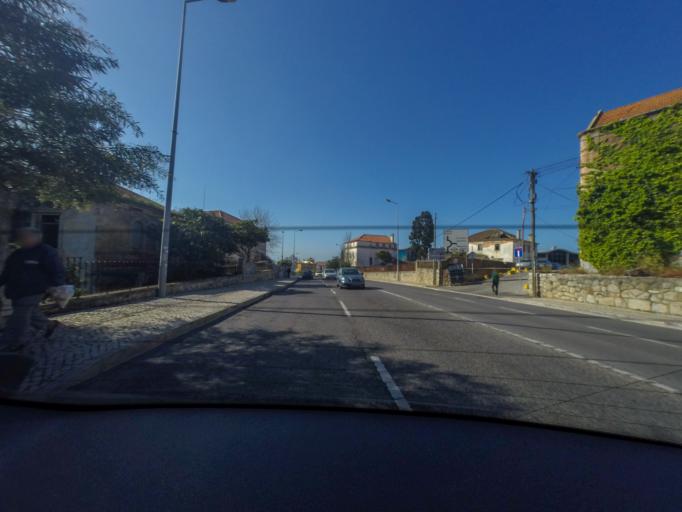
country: PT
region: Lisbon
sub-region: Cascais
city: Monte Estoril
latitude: 38.7027
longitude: -9.4178
